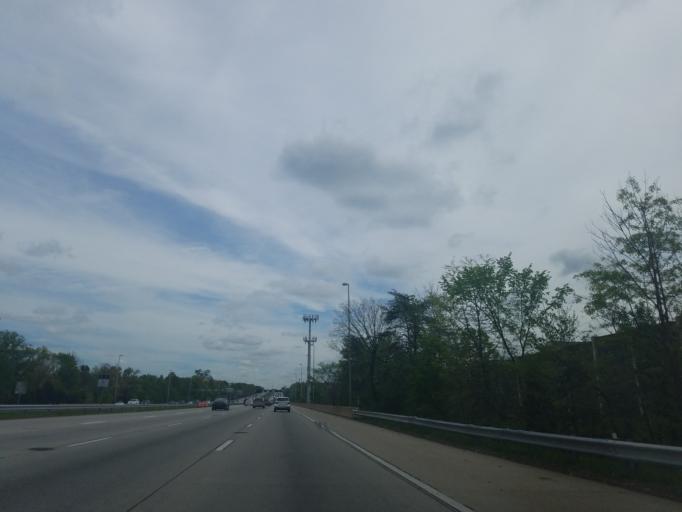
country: US
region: Virginia
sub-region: Fairfax County
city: Centreville
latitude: 38.8489
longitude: -77.4188
